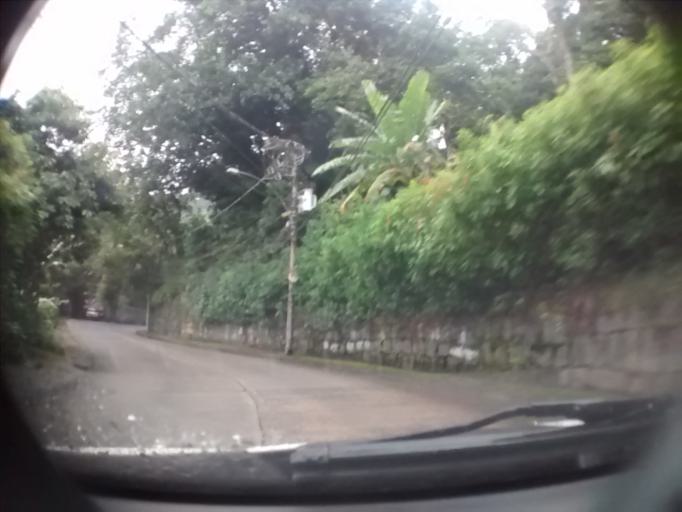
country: BR
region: Rio de Janeiro
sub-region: Rio De Janeiro
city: Rio de Janeiro
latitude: -22.9722
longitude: -43.2810
